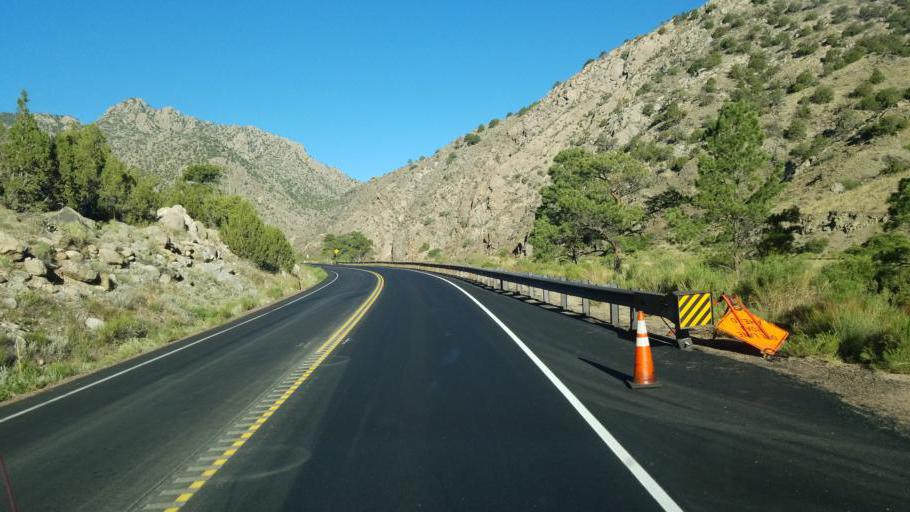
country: US
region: Colorado
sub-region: Fremont County
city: Canon City
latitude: 38.4579
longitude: -105.4826
